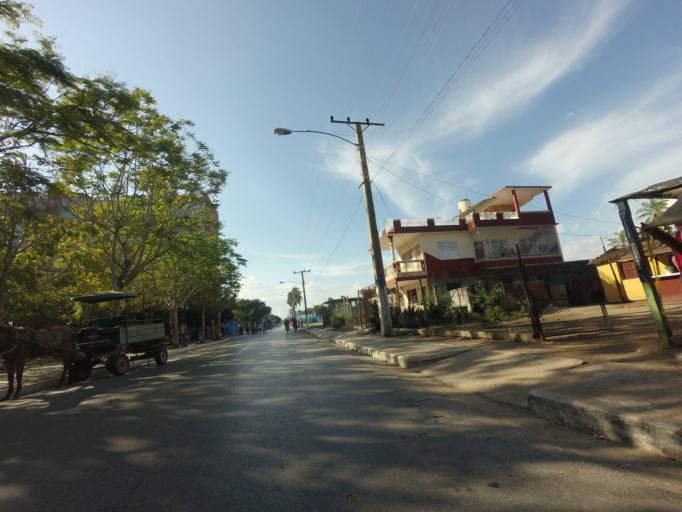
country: CU
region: Ciego de Avila
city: Ciego de Avila
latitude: 21.8451
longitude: -78.7654
